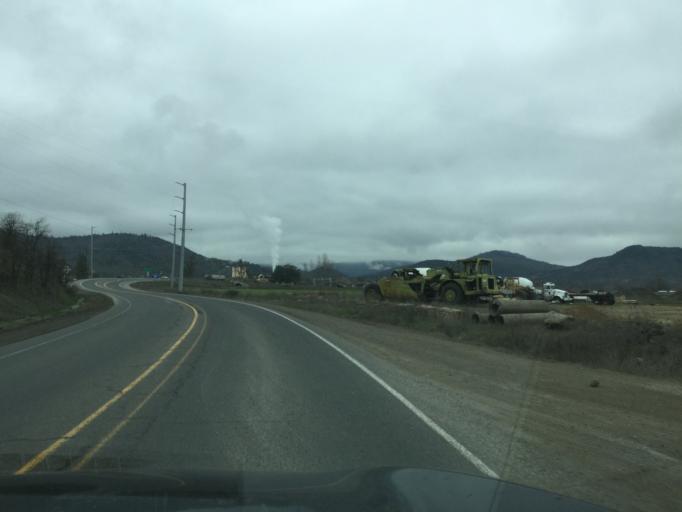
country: US
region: Oregon
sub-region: Jackson County
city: Central Point
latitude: 42.4192
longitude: -122.9538
